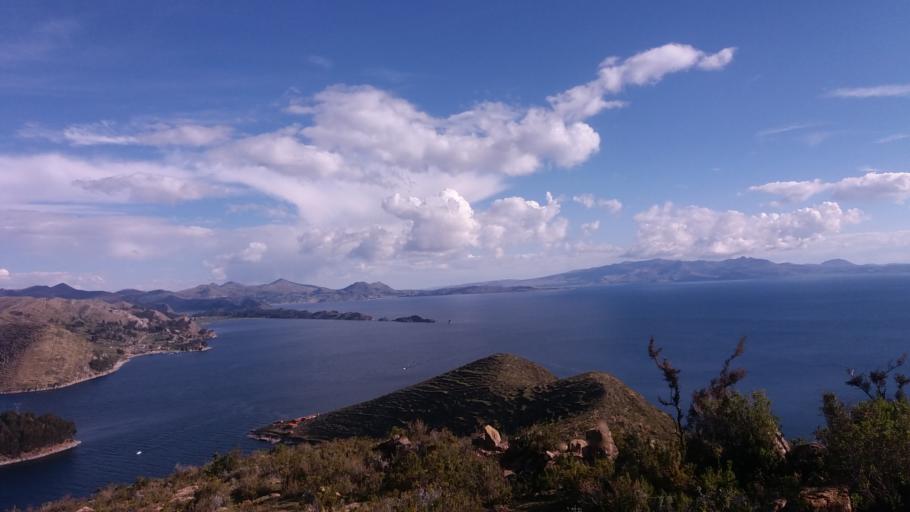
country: BO
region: La Paz
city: Yumani
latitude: -16.0425
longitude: -69.1470
